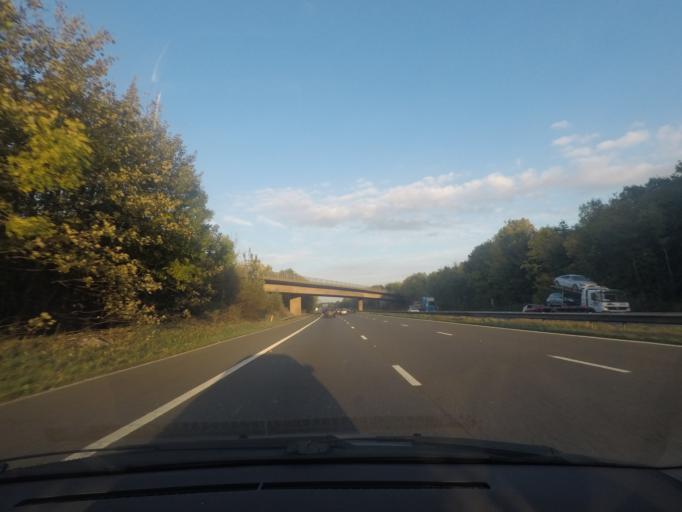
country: GB
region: England
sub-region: North Lincolnshire
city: Scawby
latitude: 53.5498
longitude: -0.5256
